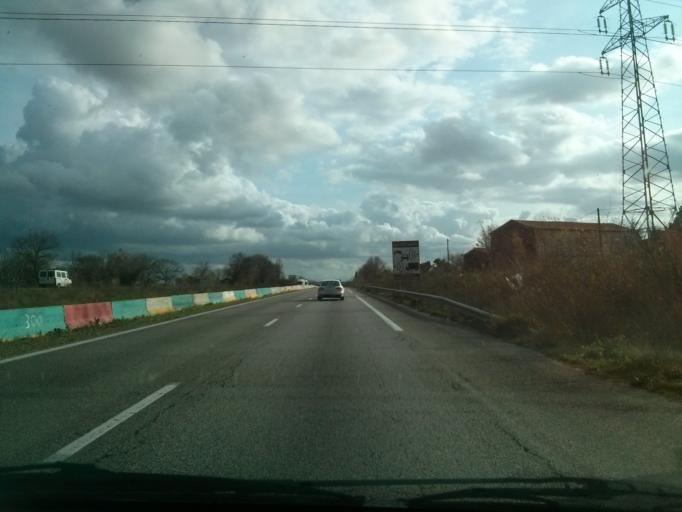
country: FR
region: Provence-Alpes-Cote d'Azur
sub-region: Departement des Bouches-du-Rhone
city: Arles
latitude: 43.6585
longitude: 4.6465
